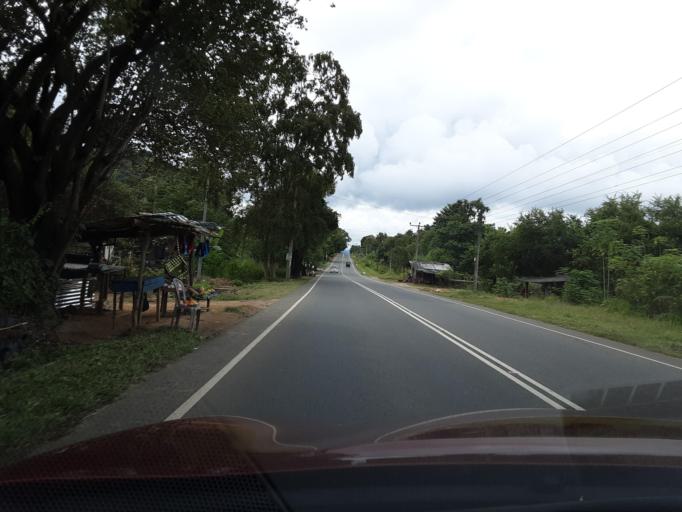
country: LK
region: Uva
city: Badulla
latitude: 7.3970
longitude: 81.1180
